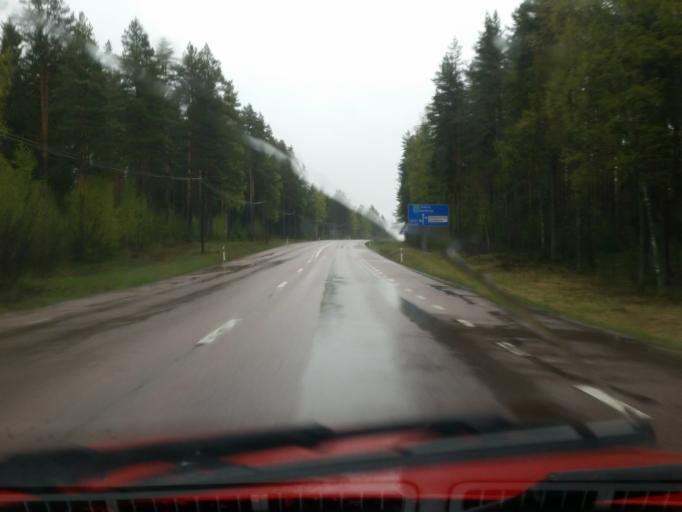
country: SE
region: Dalarna
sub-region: Borlange Kommun
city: Borlaenge
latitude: 60.5301
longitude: 15.3204
